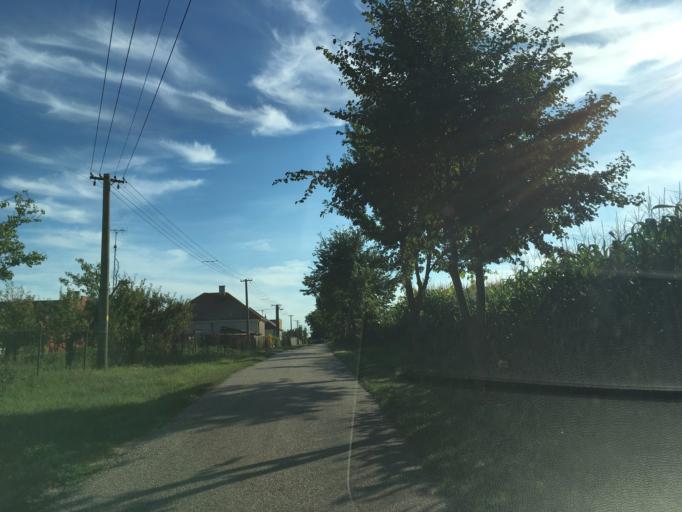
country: SK
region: Nitriansky
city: Svodin
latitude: 47.8996
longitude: 18.4081
